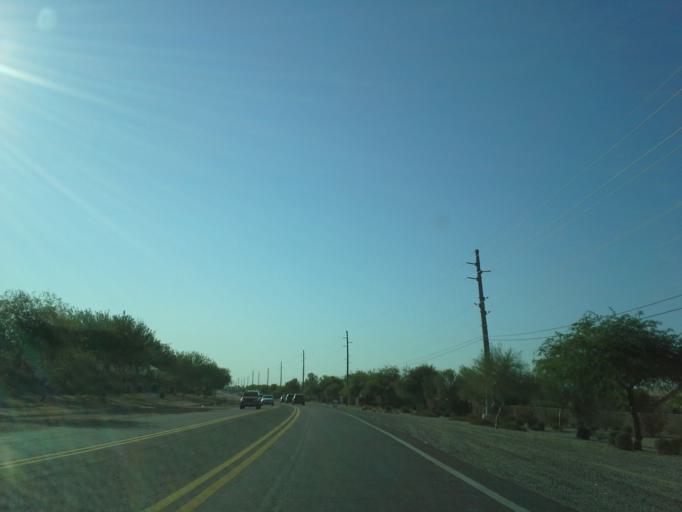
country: US
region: Arizona
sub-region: Pinal County
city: San Tan Valley
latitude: 33.1682
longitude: -111.5690
